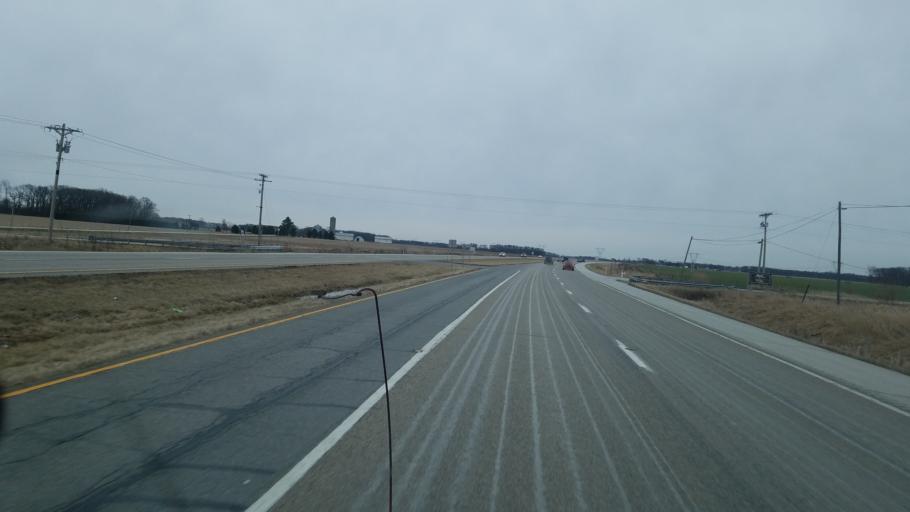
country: US
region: Indiana
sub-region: LaPorte County
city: Wanatah
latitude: 41.4328
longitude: -86.8151
